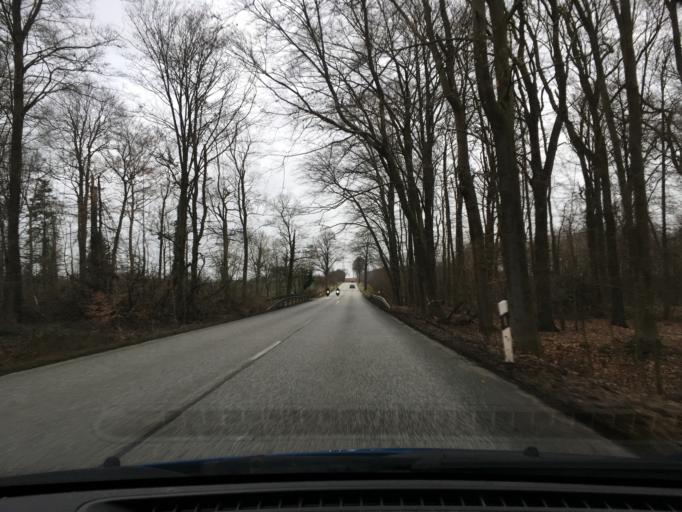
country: DE
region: Schleswig-Holstein
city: Schulendorf
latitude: 53.4800
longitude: 10.5295
